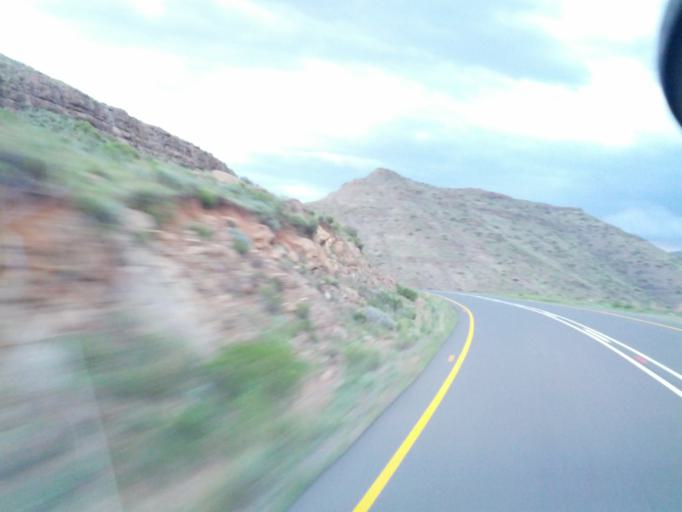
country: LS
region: Qacha's Nek
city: Qacha's Nek
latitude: -30.0393
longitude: 28.3076
